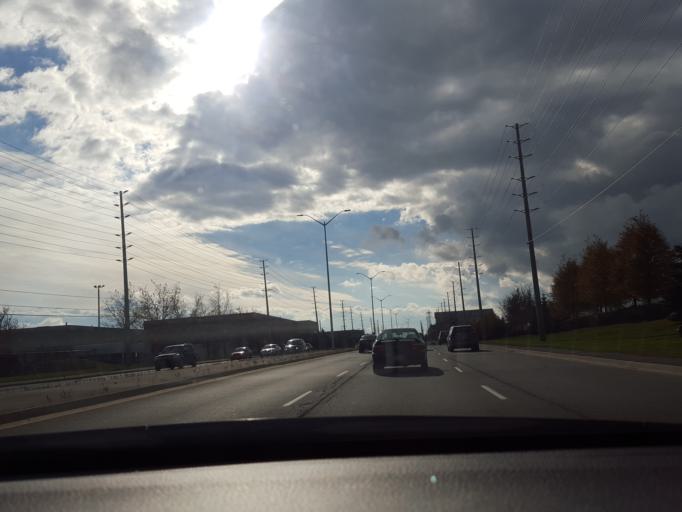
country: CA
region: Ontario
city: Brampton
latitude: 43.6546
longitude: -79.6968
